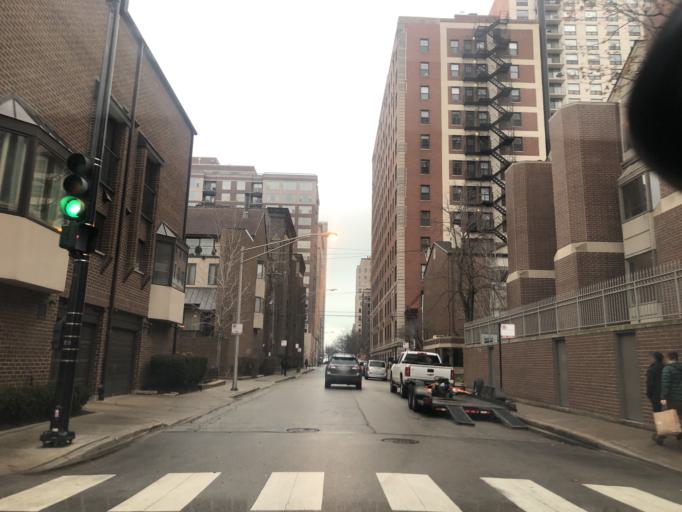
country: US
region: Illinois
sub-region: Cook County
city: Chicago
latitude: 41.9058
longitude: -87.6315
